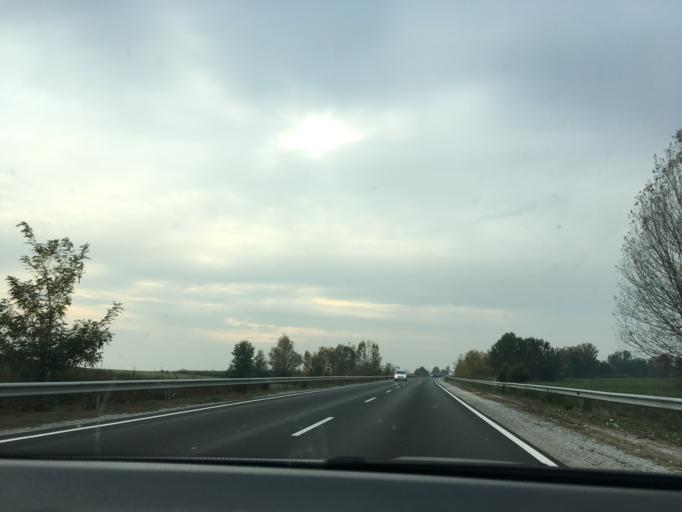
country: HU
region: Pest
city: Abony
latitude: 47.2021
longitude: 19.9529
